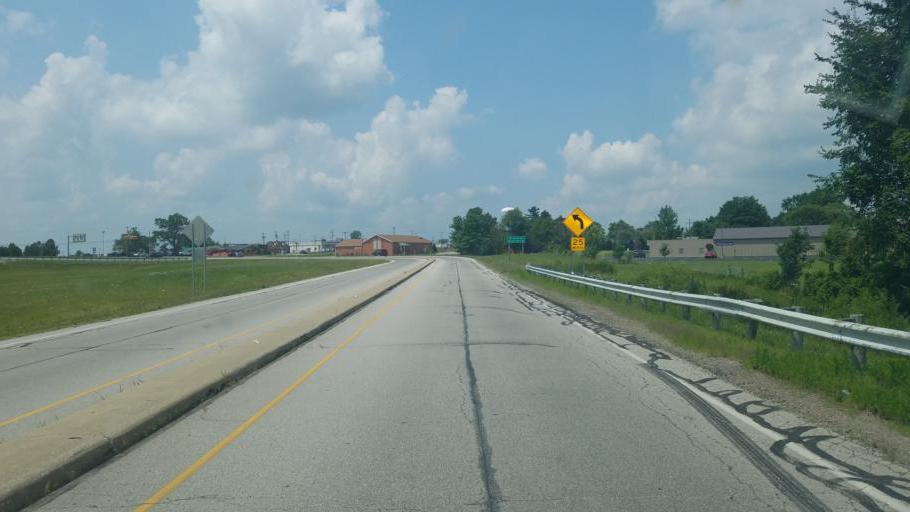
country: US
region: Ohio
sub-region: Richland County
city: Ontario
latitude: 40.7729
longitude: -82.5814
